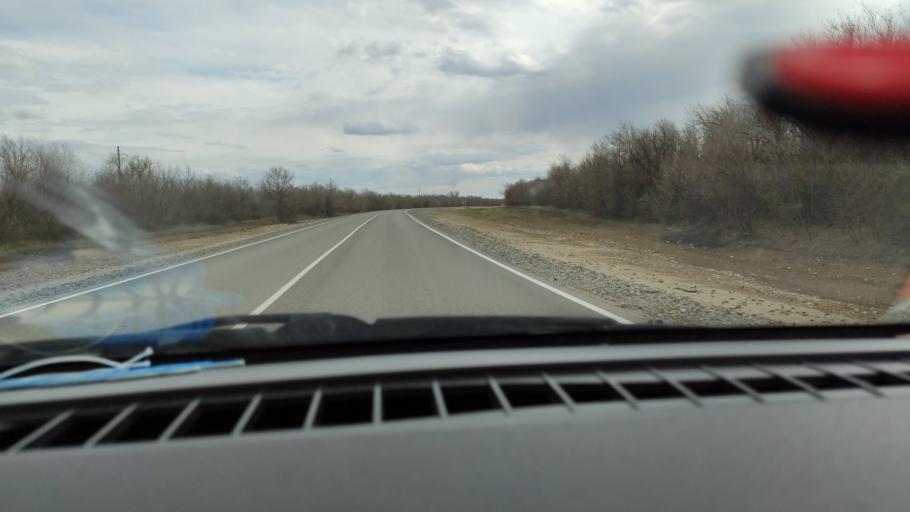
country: RU
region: Saratov
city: Privolzhskiy
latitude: 51.1503
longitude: 45.9625
